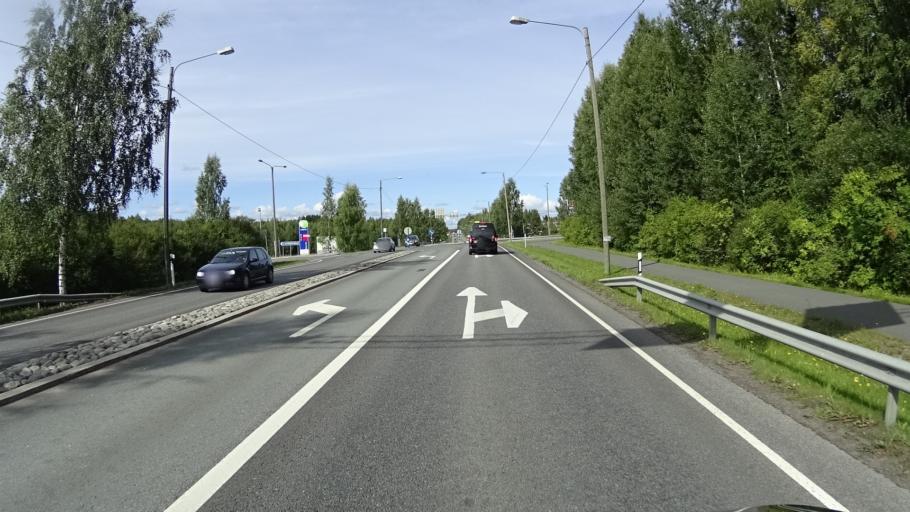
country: FI
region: Pirkanmaa
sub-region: Tampere
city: Haemeenkyroe
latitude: 61.6440
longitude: 23.1891
